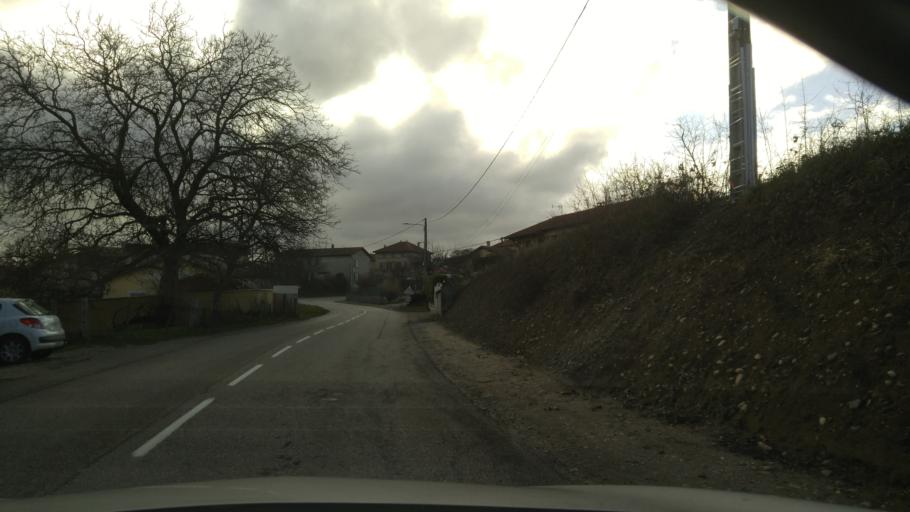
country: FR
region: Rhone-Alpes
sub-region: Departement de l'Isere
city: Roche
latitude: 45.5879
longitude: 5.1624
